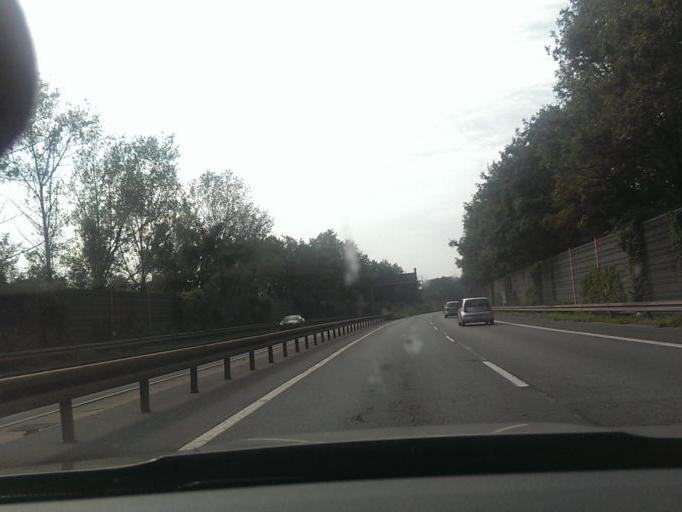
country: DE
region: Lower Saxony
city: Isernhagen Farster Bauerschaft
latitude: 52.4024
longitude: 9.8151
